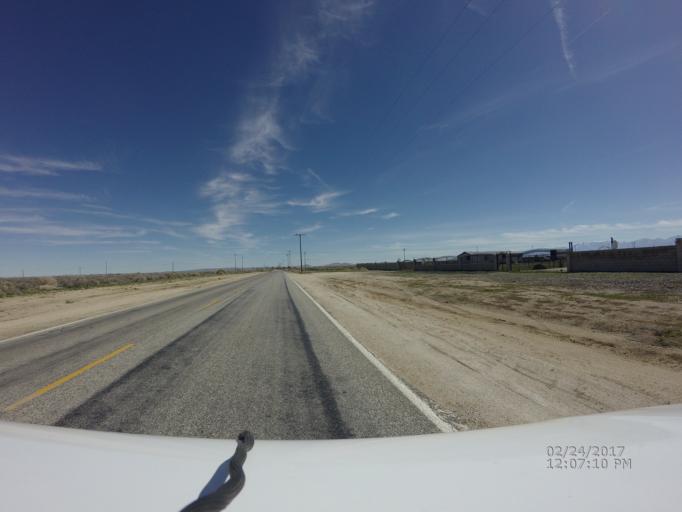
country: US
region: California
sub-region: Los Angeles County
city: Lancaster
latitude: 34.7191
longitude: -118.0432
